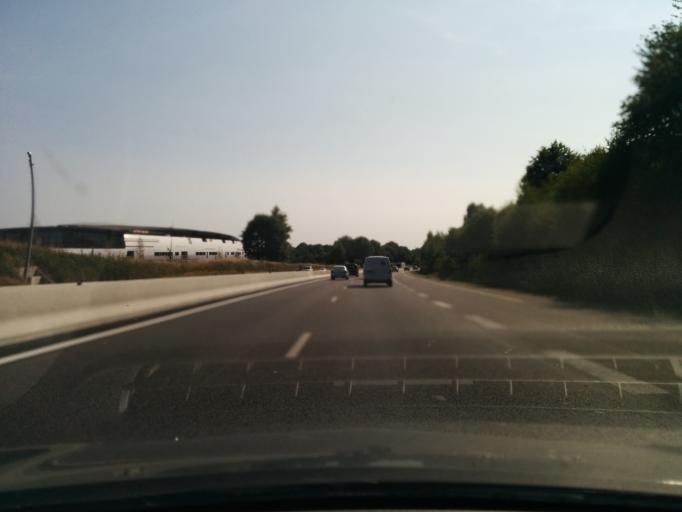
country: FR
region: Limousin
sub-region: Departement de la Haute-Vienne
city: Limoges
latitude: 45.8578
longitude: 1.2831
